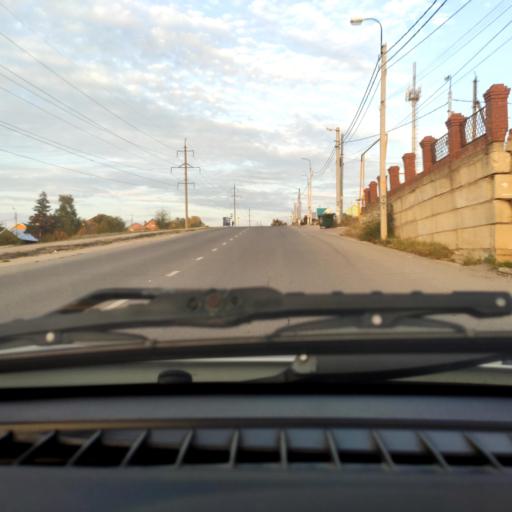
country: RU
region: Samara
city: Zhigulevsk
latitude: 53.4841
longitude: 49.5305
